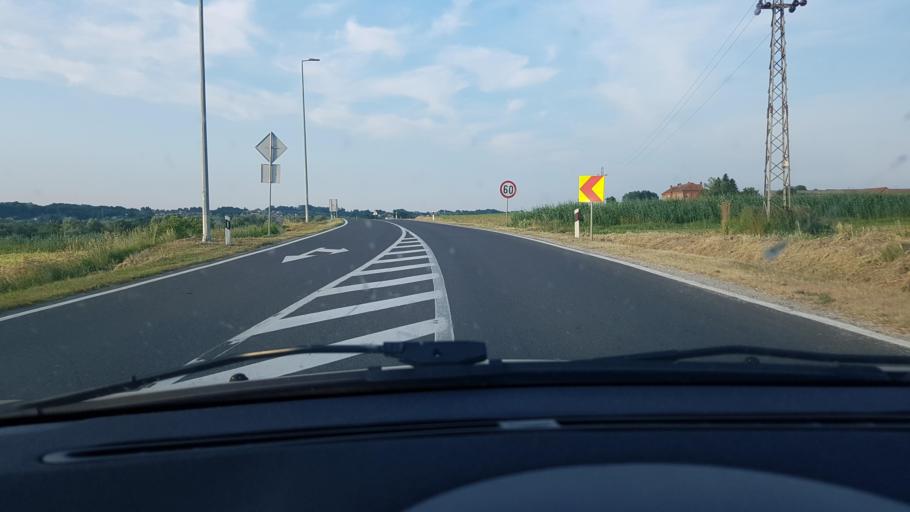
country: HR
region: Varazdinska
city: Lepoglava
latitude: 46.2204
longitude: 16.0711
